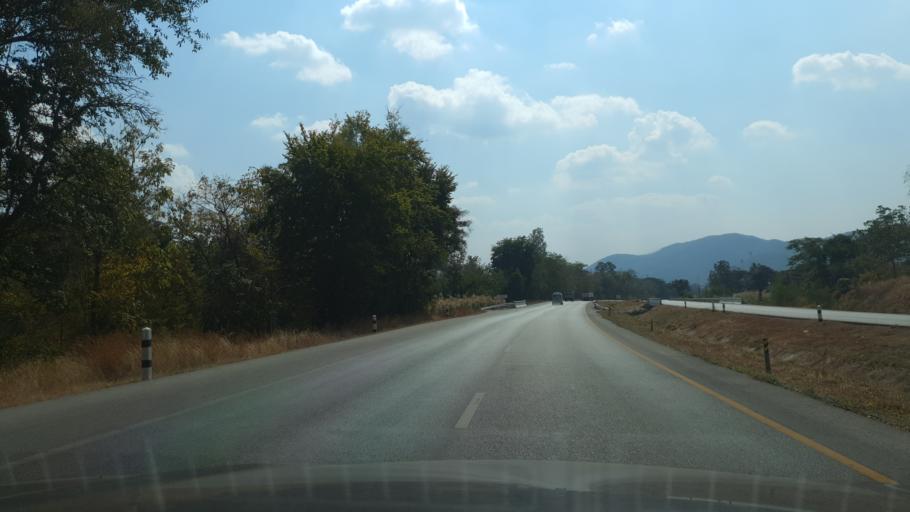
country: TH
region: Lampang
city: Mae Phrik
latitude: 17.3765
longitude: 99.1492
